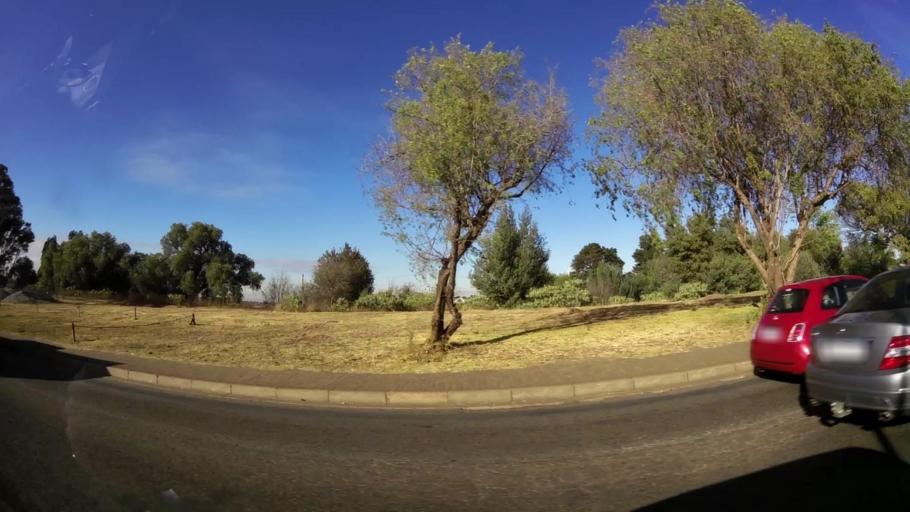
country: ZA
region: Gauteng
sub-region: West Rand District Municipality
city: Krugersdorp
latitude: -26.1197
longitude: 27.8155
